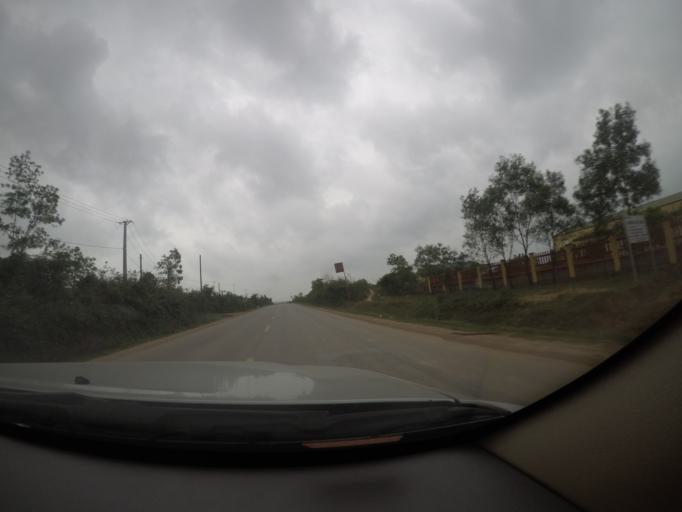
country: VN
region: Quang Tri
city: Dong Ha
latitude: 16.7920
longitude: 107.0528
